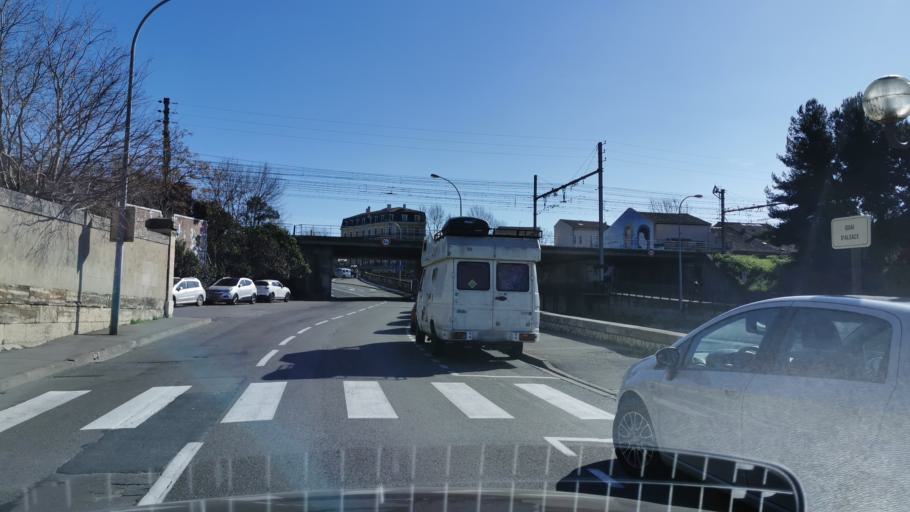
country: FR
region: Languedoc-Roussillon
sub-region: Departement de l'Aude
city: Narbonne
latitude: 43.1862
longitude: 2.9988
